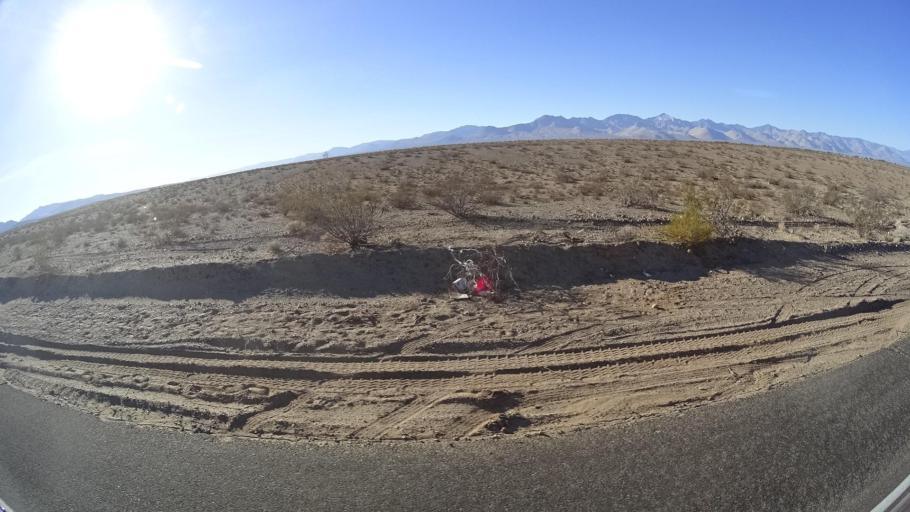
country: US
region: California
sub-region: Kern County
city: China Lake Acres
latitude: 35.6165
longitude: -117.7230
